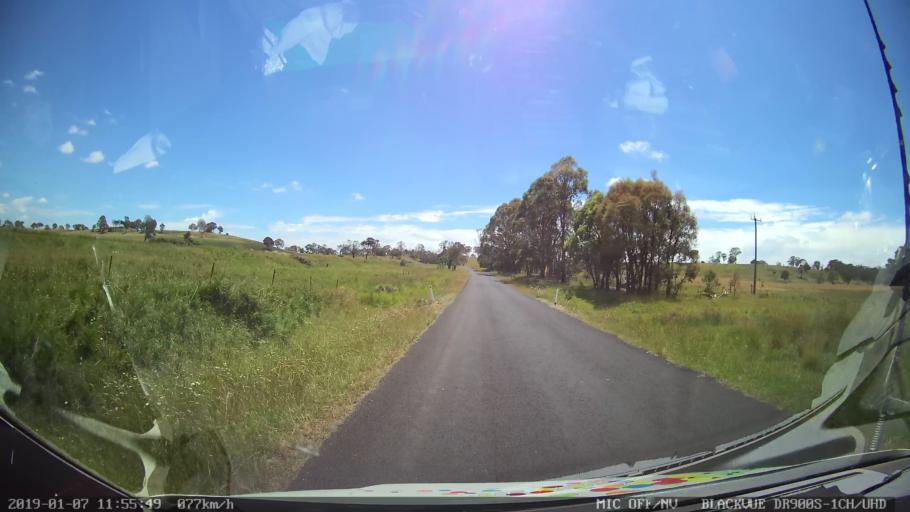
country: AU
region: New South Wales
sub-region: Guyra
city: Guyra
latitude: -30.2814
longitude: 151.6721
